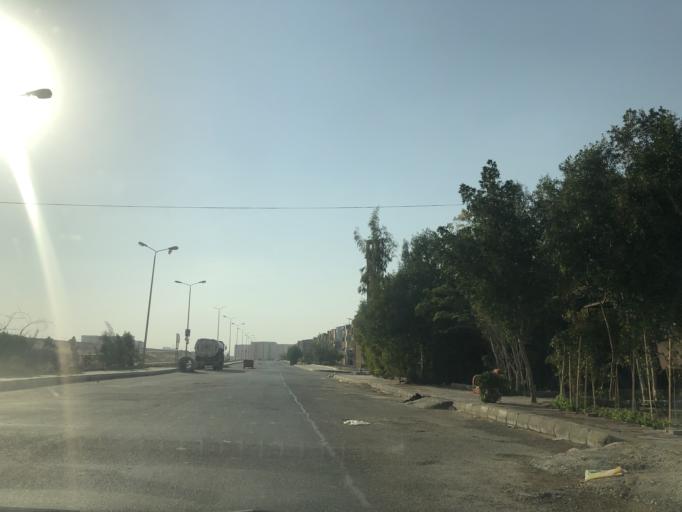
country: EG
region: Al Jizah
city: Madinat Sittah Uktubar
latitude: 29.9040
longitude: 30.9285
